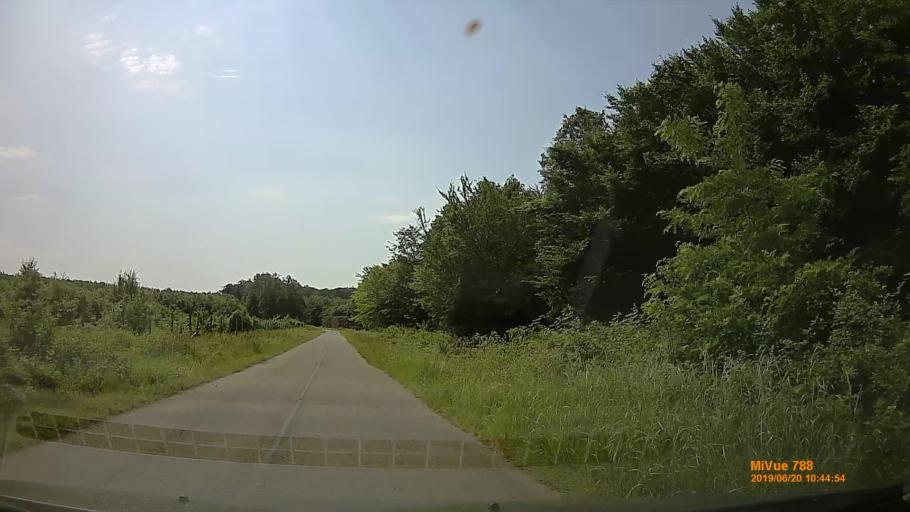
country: HU
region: Baranya
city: Hidas
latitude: 46.1858
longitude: 18.5682
